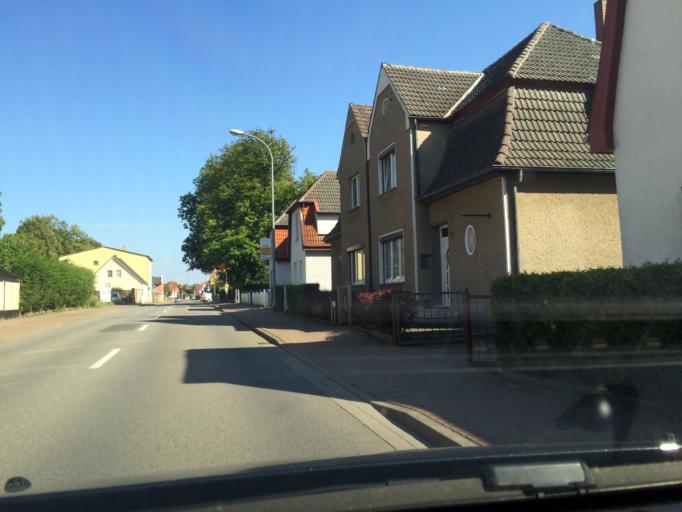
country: DE
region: Mecklenburg-Vorpommern
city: Barth
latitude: 54.3627
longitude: 12.7297
